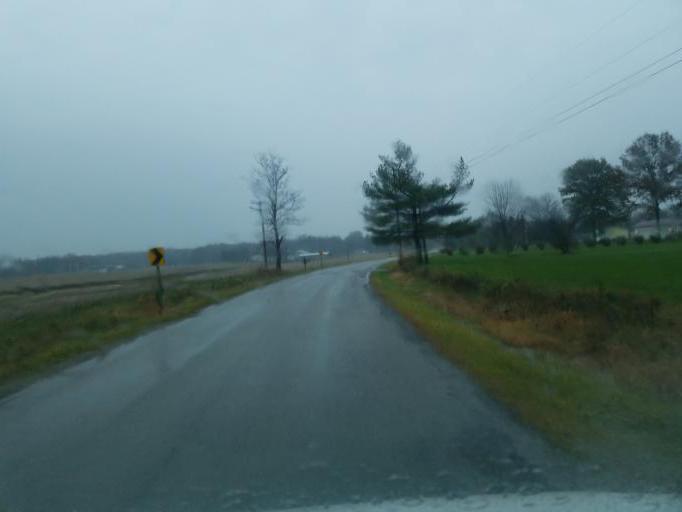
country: US
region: Ohio
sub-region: Delaware County
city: Sunbury
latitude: 40.3585
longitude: -82.8368
